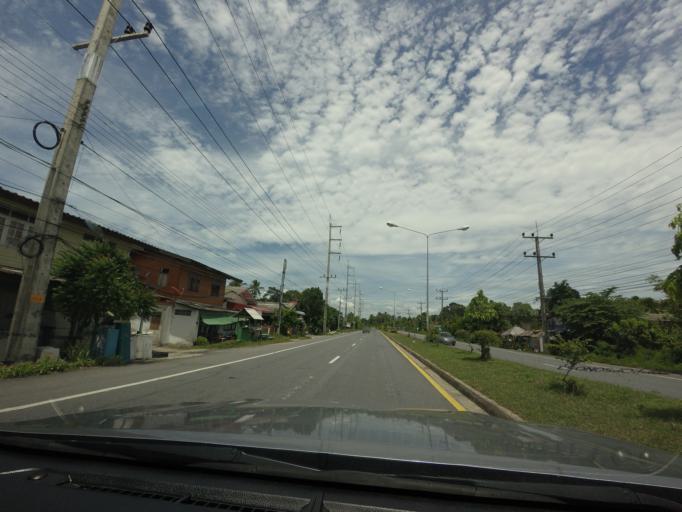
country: TH
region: Songkhla
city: Krasae Sin
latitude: 7.5676
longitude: 100.4108
